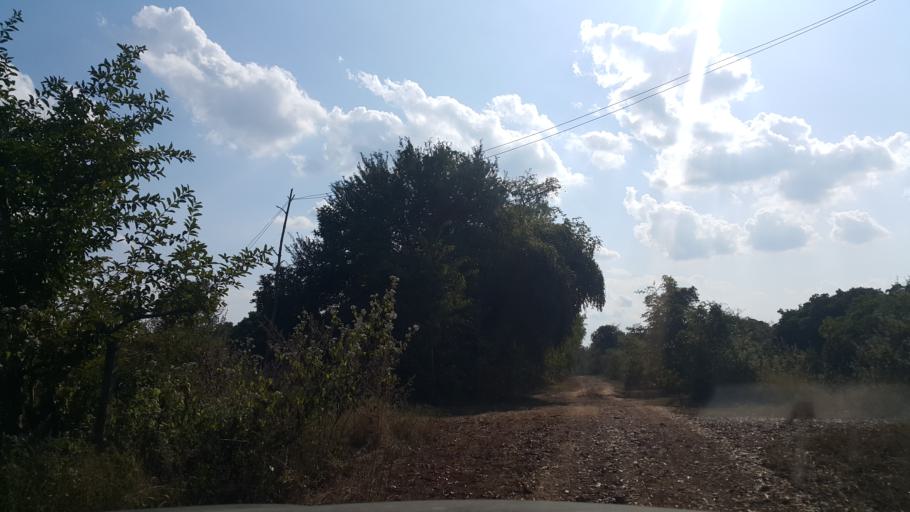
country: TH
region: Lamphun
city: Ban Thi
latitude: 18.5659
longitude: 99.1185
